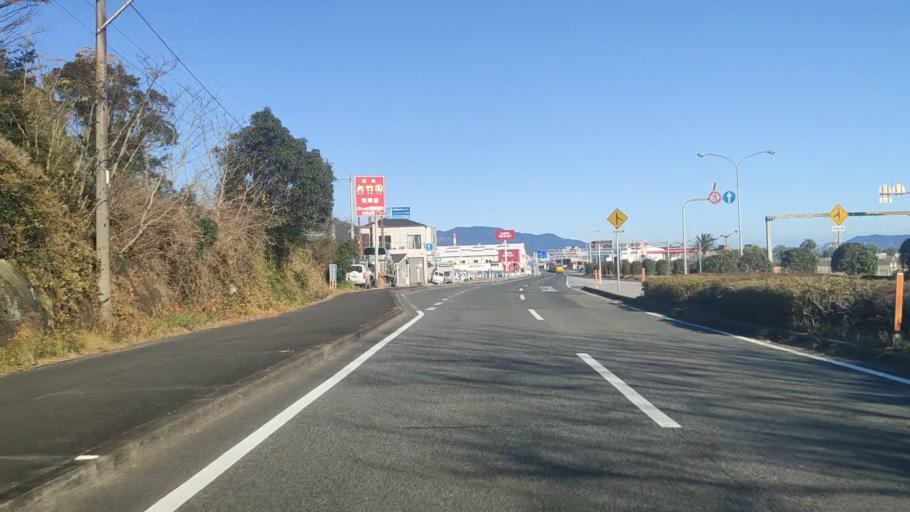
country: JP
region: Miyazaki
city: Nobeoka
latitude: 32.5401
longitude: 131.6785
